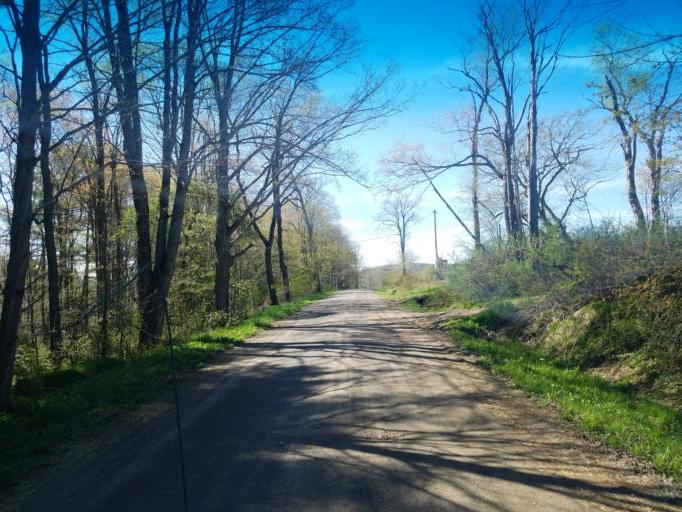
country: US
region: New York
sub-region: Allegany County
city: Andover
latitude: 41.9634
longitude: -77.7819
